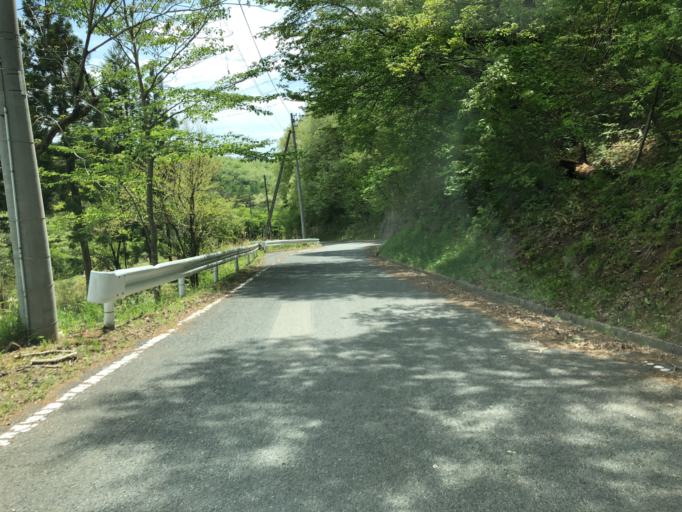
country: JP
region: Miyagi
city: Marumori
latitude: 37.6966
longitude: 140.7788
